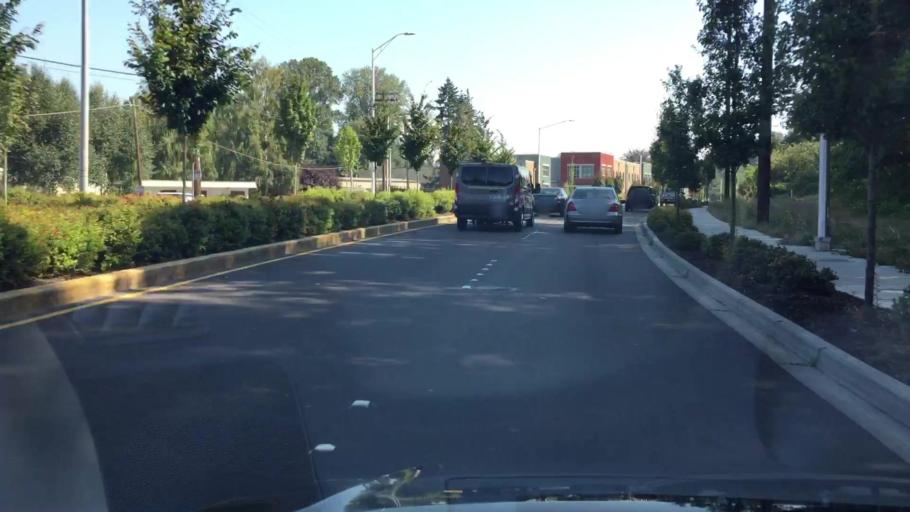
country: US
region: Washington
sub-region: King County
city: Tukwila
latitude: 47.4744
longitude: -122.2565
